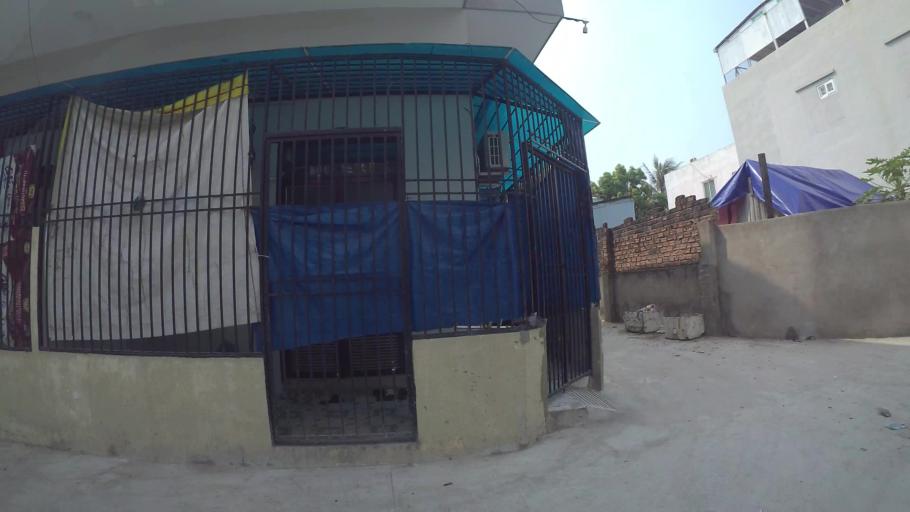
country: VN
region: Da Nang
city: Son Tra
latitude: 16.0453
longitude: 108.2462
